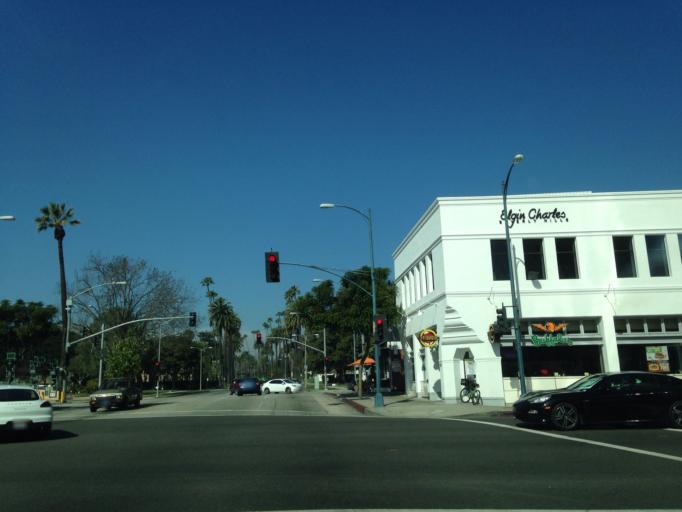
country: US
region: California
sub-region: Los Angeles County
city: Beverly Hills
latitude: 34.0712
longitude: -118.4032
